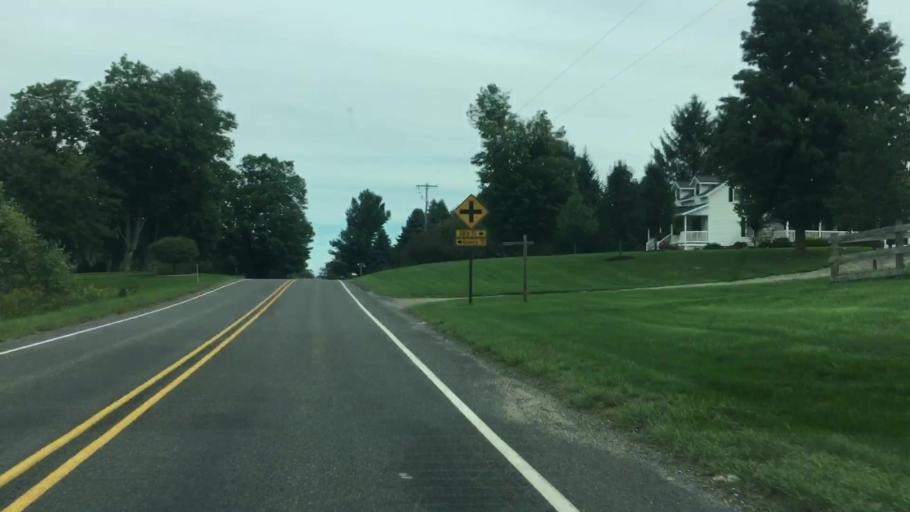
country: US
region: Michigan
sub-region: Kent County
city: Byron Center
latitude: 42.8389
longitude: -85.7825
